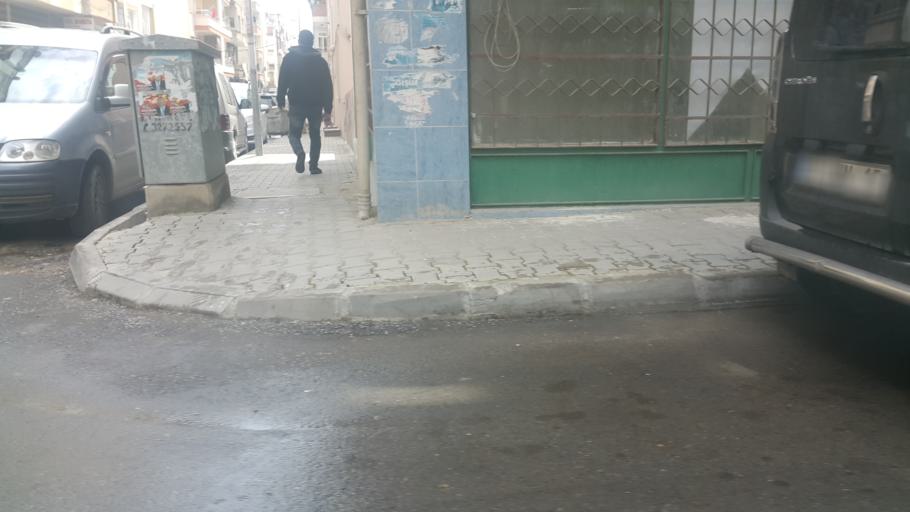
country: TR
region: Mersin
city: Mercin
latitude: 36.8063
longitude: 34.6262
